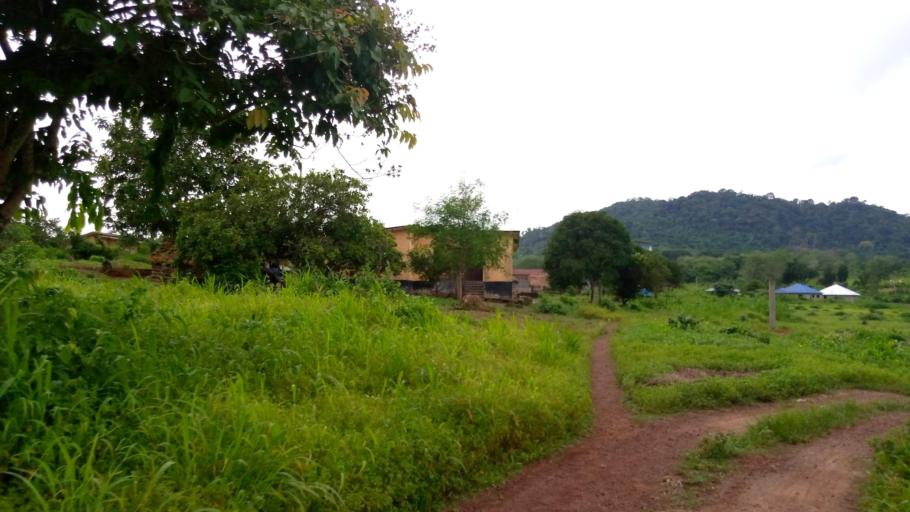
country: SL
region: Southern Province
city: Moyamba
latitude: 8.1632
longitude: -12.4468
